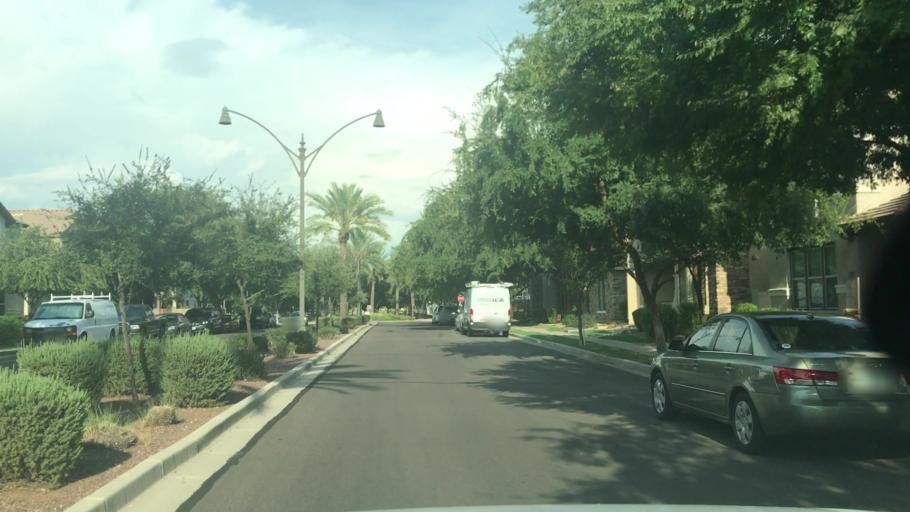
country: US
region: Arizona
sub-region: Maricopa County
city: Gilbert
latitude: 33.3250
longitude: -111.7187
